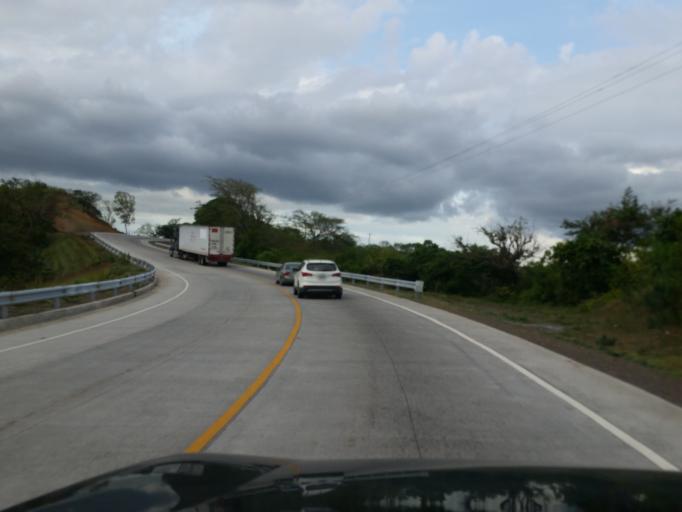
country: NI
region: Managua
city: Ciudad Sandino
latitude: 12.0759
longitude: -86.4272
